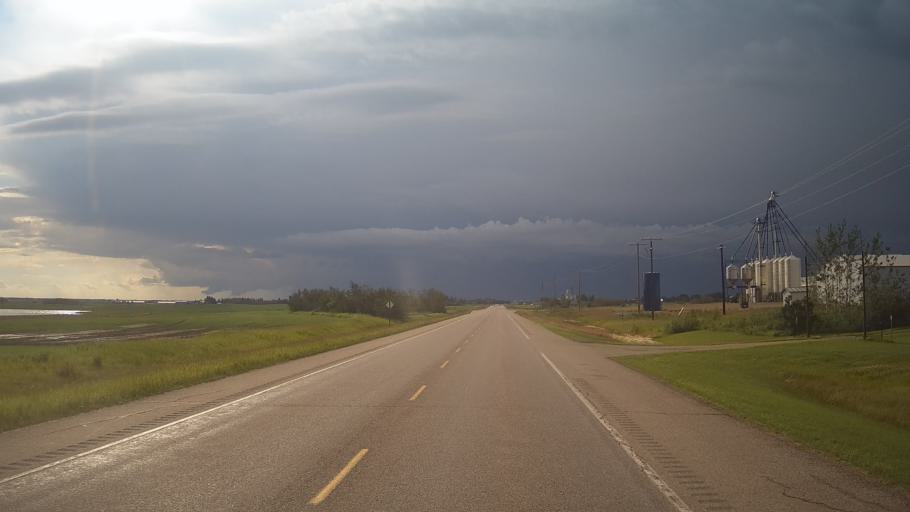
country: CA
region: Alberta
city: Vegreville
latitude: 53.2235
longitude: -112.2238
